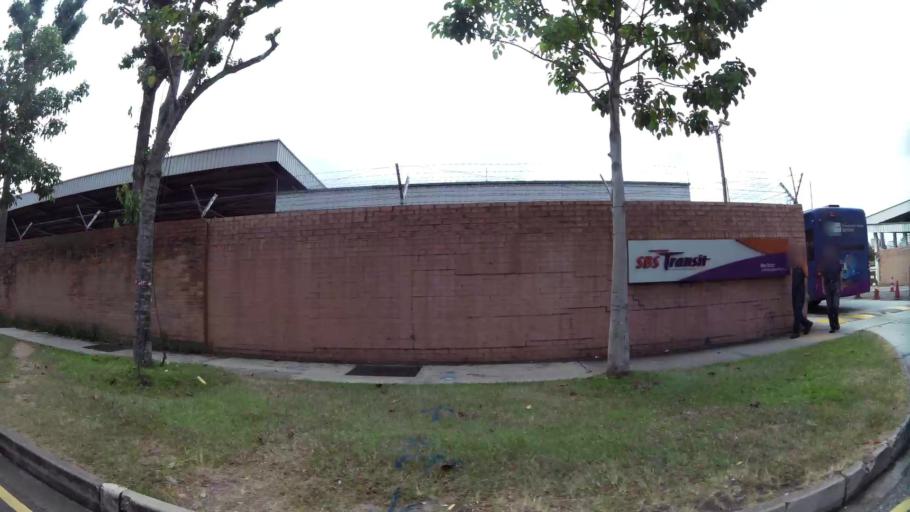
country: SG
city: Singapore
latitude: 1.3410
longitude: 103.7548
